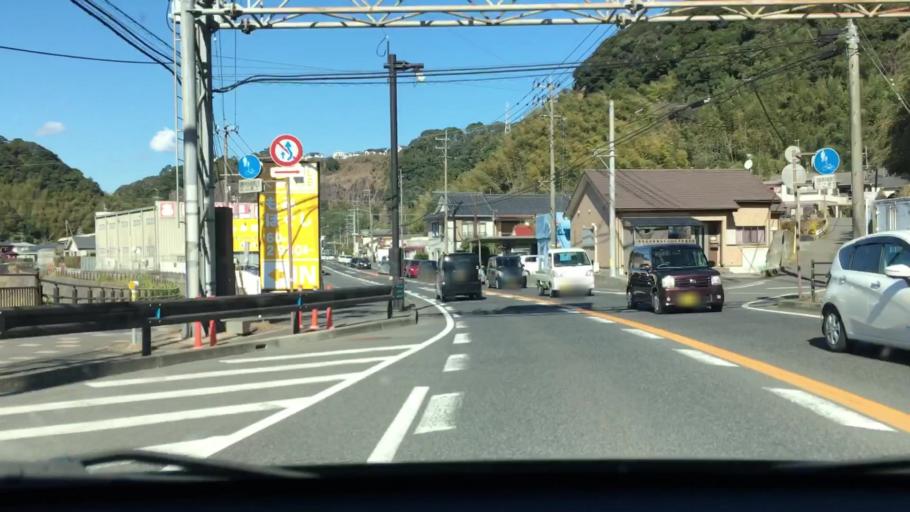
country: JP
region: Kagoshima
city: Kagoshima-shi
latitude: 31.6290
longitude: 130.5250
